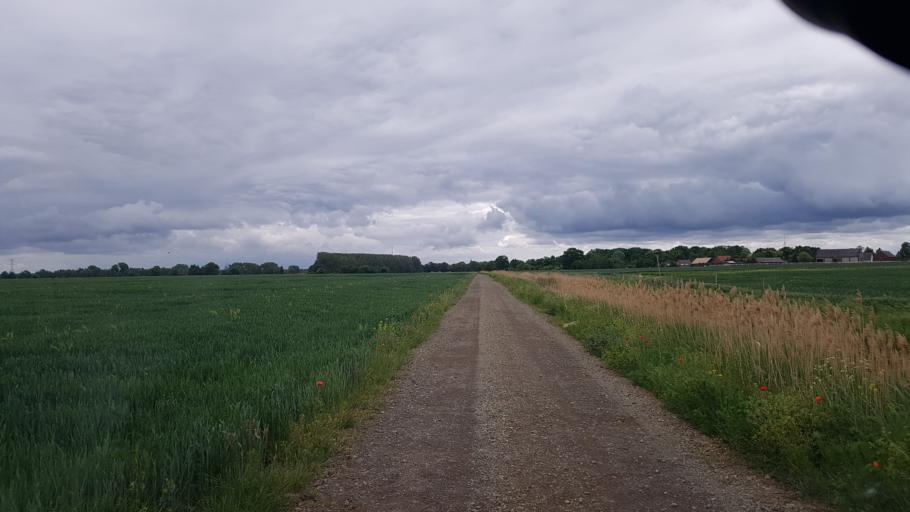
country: DE
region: Brandenburg
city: Doberlug-Kirchhain
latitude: 51.6581
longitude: 13.5457
